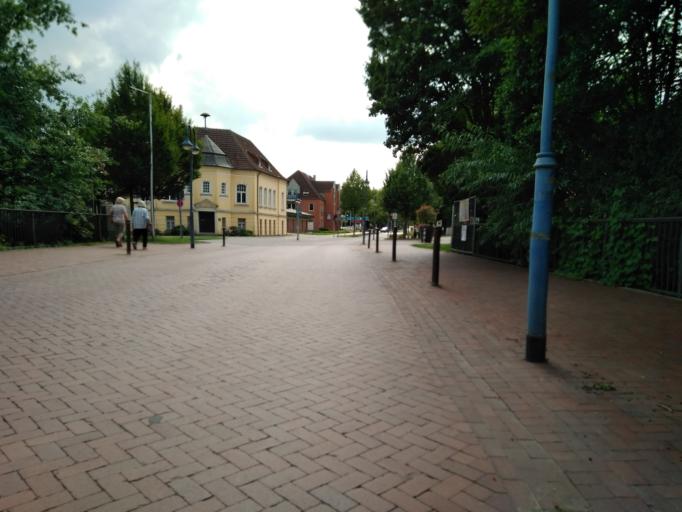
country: DE
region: North Rhine-Westphalia
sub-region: Regierungsbezirk Dusseldorf
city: Schermbeck
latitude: 51.6915
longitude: 6.8685
